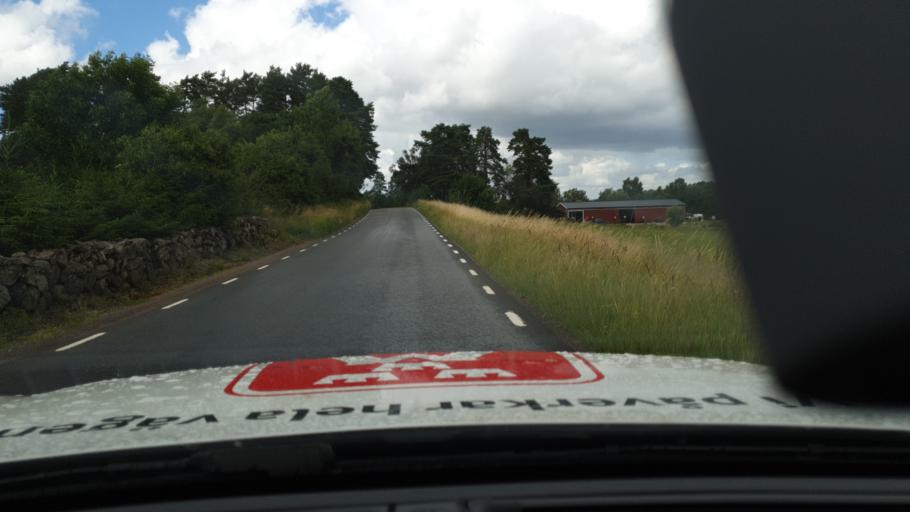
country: SE
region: Vaestra Goetaland
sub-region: Falkopings Kommun
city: Akarp
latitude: 58.2561
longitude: 13.5980
